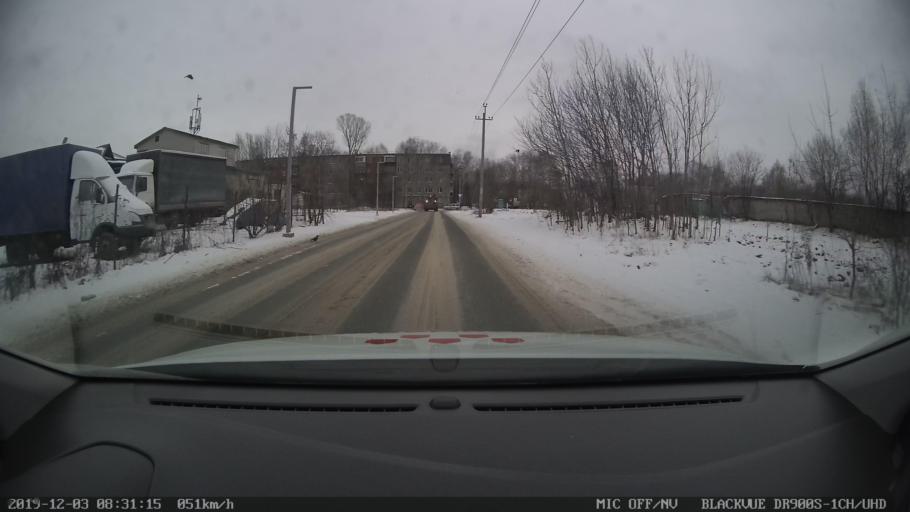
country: RU
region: Tatarstan
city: Staroye Arakchino
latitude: 55.8774
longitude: 49.0130
